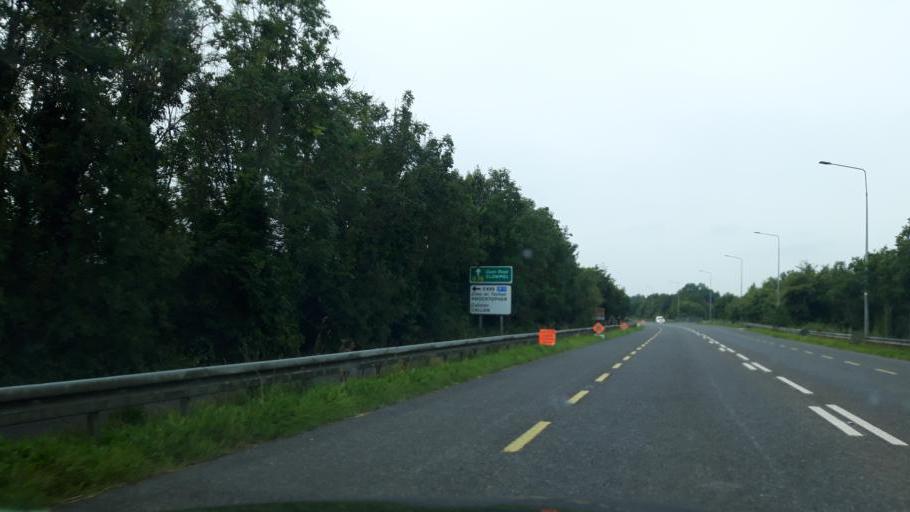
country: IE
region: Leinster
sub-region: Kilkenny
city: Callan
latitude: 52.5482
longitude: -7.3935
